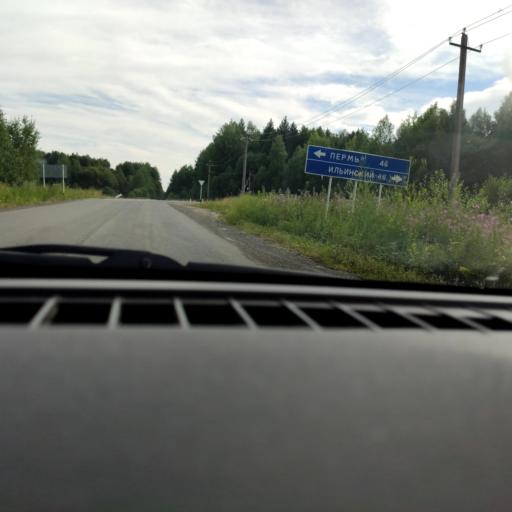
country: RU
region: Perm
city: Polazna
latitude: 58.3160
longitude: 56.1488
